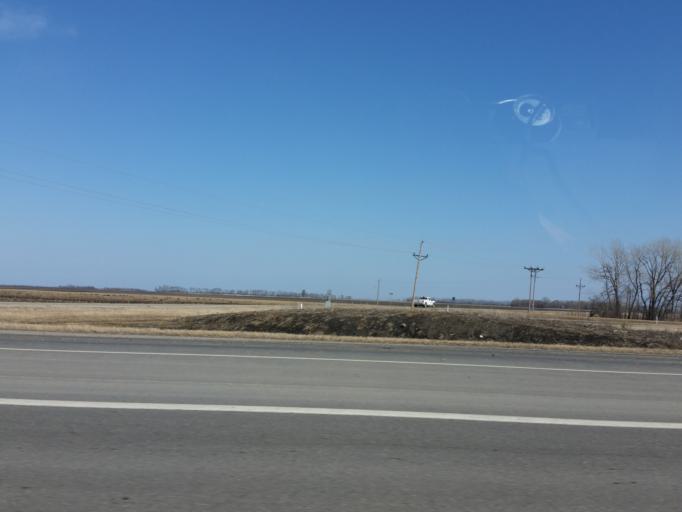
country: US
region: North Dakota
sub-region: Walsh County
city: Grafton
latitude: 48.2088
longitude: -97.3429
